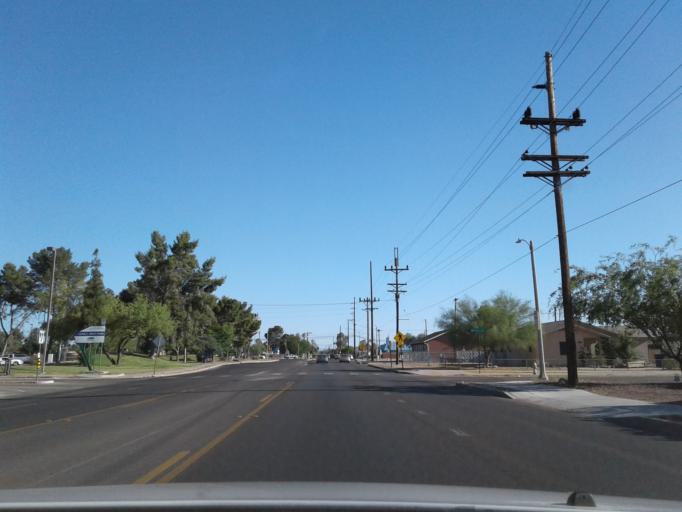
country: US
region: Arizona
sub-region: Pima County
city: Tucson
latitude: 32.2092
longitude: -110.9267
